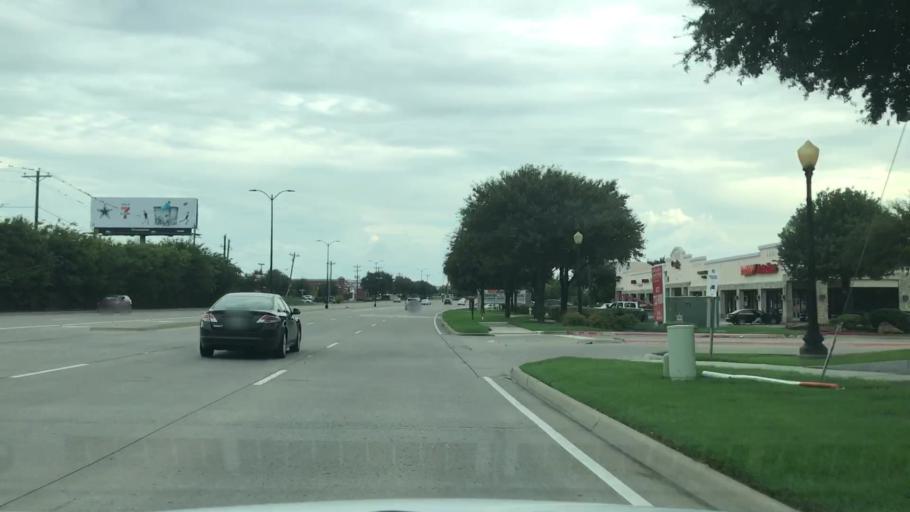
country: US
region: Texas
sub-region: Collin County
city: Frisco
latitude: 33.1358
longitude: -96.8044
